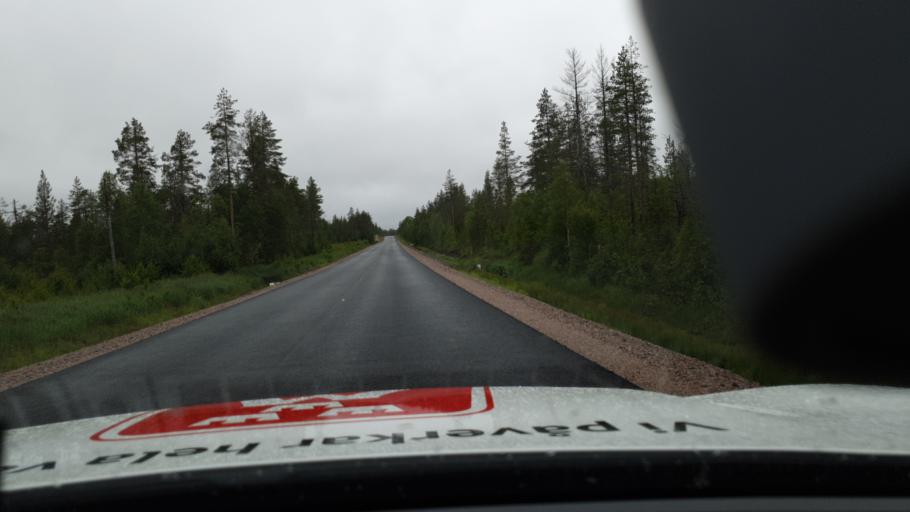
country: SE
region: Norrbotten
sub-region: Overtornea Kommun
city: OEvertornea
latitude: 66.5332
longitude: 23.3658
